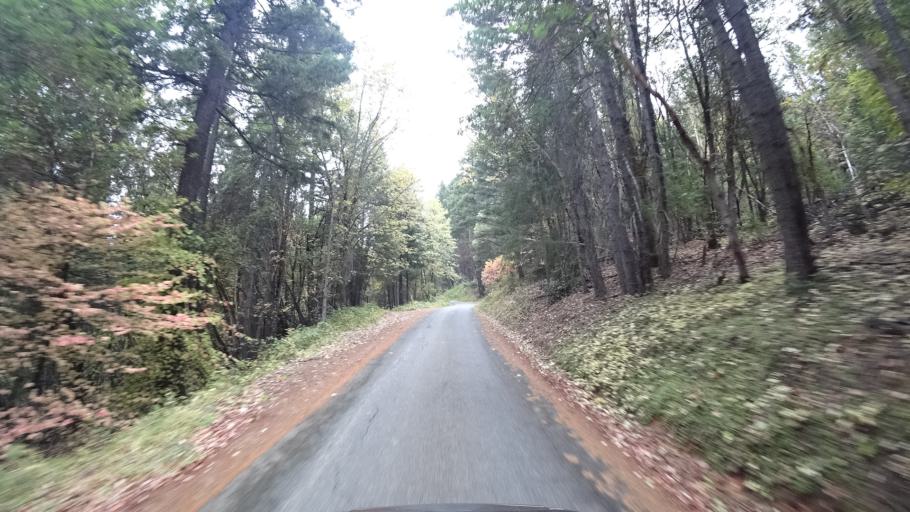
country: US
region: California
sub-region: Siskiyou County
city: Happy Camp
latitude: 41.8113
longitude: -123.3354
